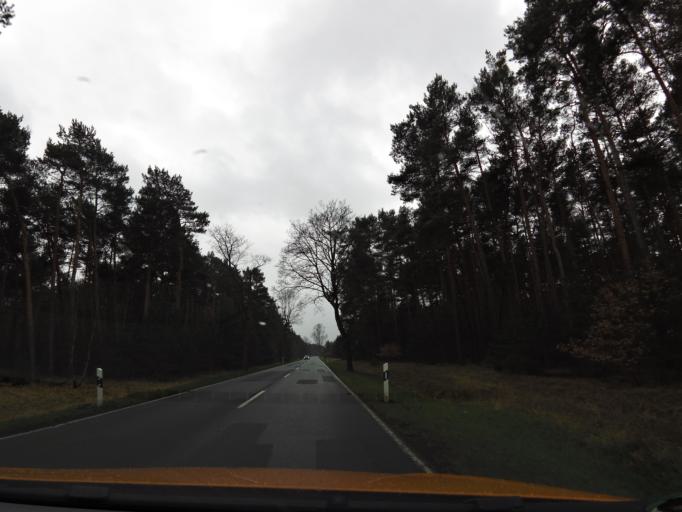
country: DE
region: Brandenburg
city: Ziesar
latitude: 52.2907
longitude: 12.3336
